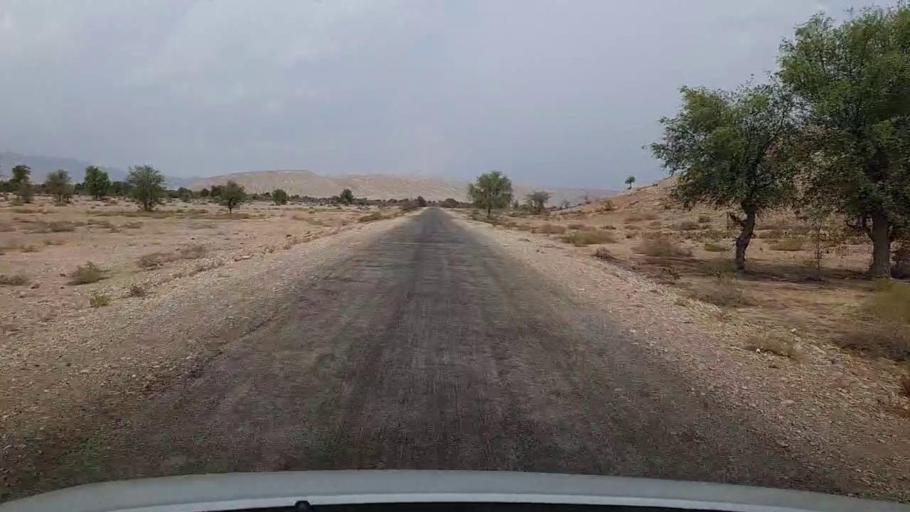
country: PK
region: Sindh
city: Sehwan
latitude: 26.2252
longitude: 67.7106
